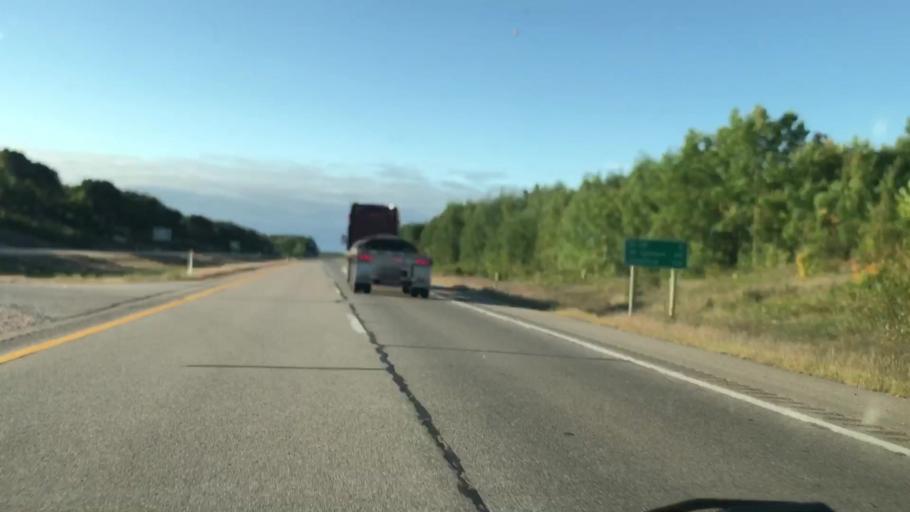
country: US
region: Michigan
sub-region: Chippewa County
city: Sault Ste. Marie
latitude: 46.4544
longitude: -84.3839
